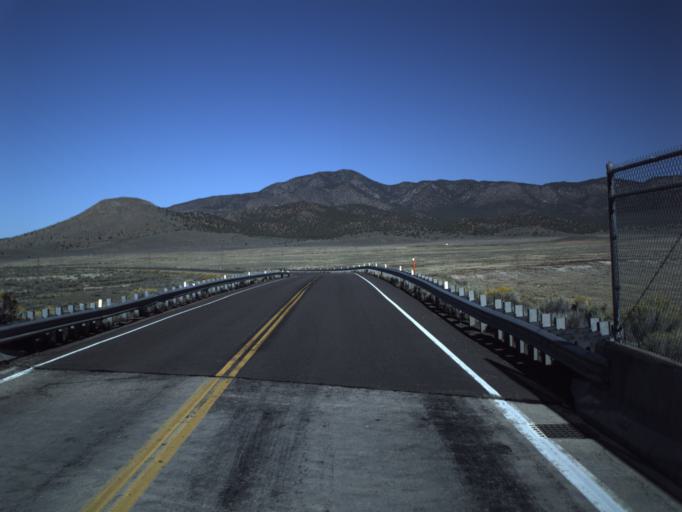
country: US
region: Utah
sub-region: Washington County
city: Enterprise
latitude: 37.8012
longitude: -113.9165
